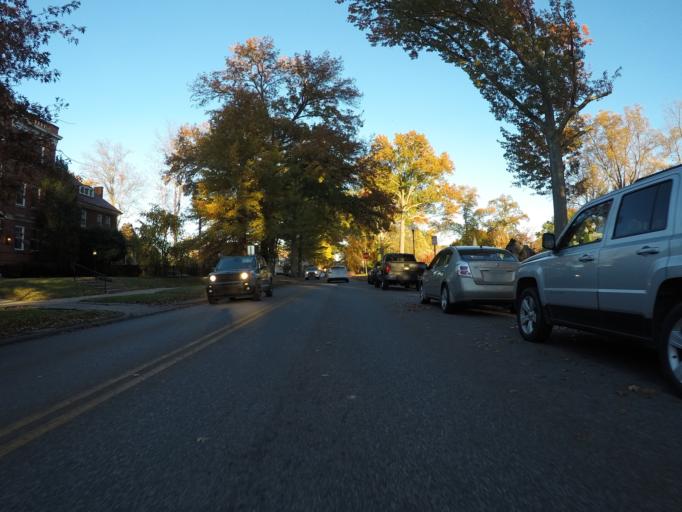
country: US
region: West Virginia
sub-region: Cabell County
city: Huntington
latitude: 38.4085
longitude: -82.4393
